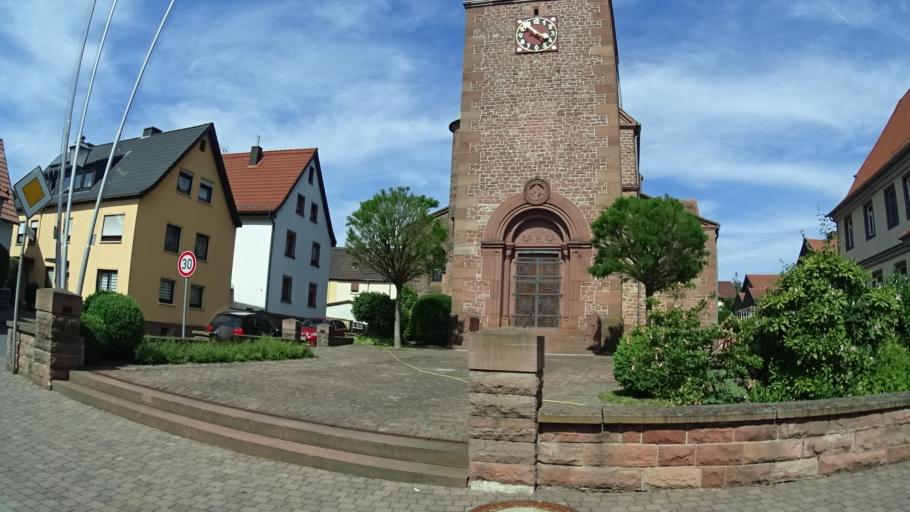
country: DE
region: Bavaria
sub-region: Regierungsbezirk Unterfranken
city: Dorfprozelten
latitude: 49.7788
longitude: 9.3801
